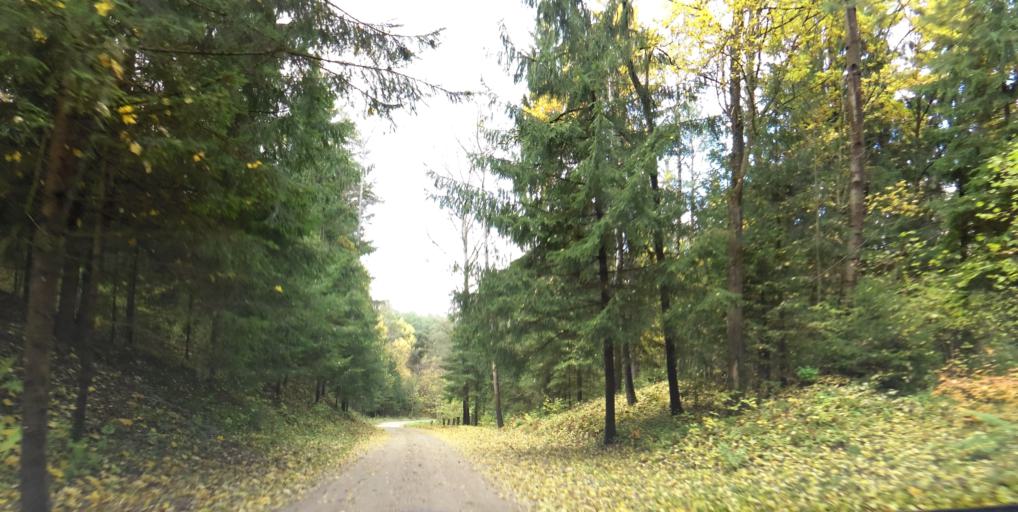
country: LT
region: Vilnius County
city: Vilkpede
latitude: 54.6496
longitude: 25.2537
